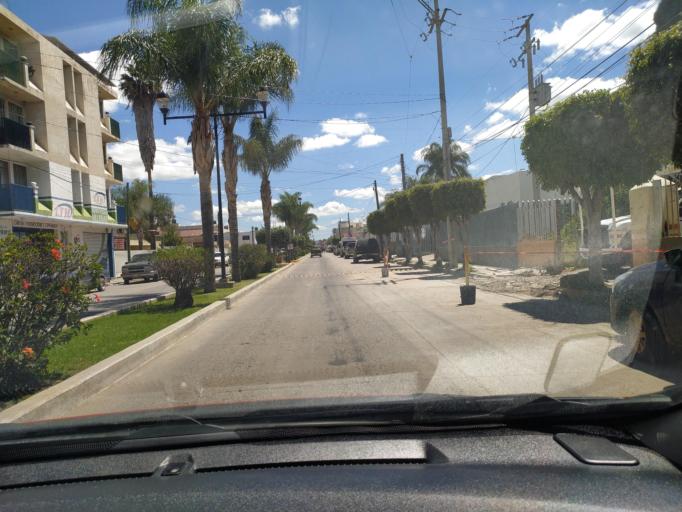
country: MX
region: Jalisco
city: San Julian
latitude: 21.0096
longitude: -102.1751
